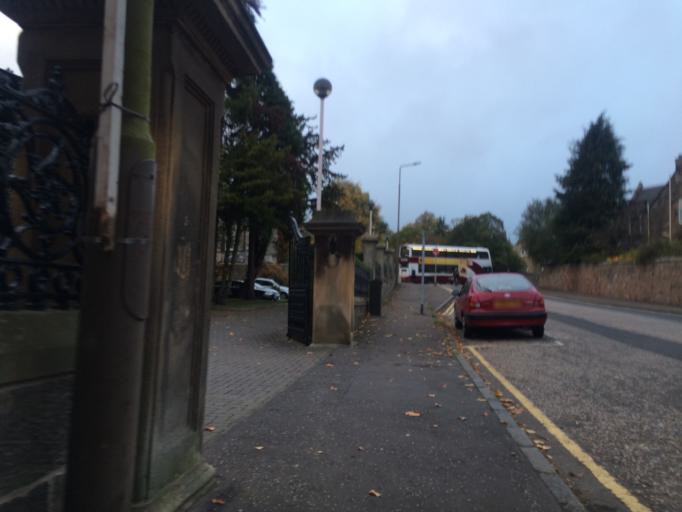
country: GB
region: Scotland
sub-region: Edinburgh
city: Edinburgh
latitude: 55.9308
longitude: -3.1912
